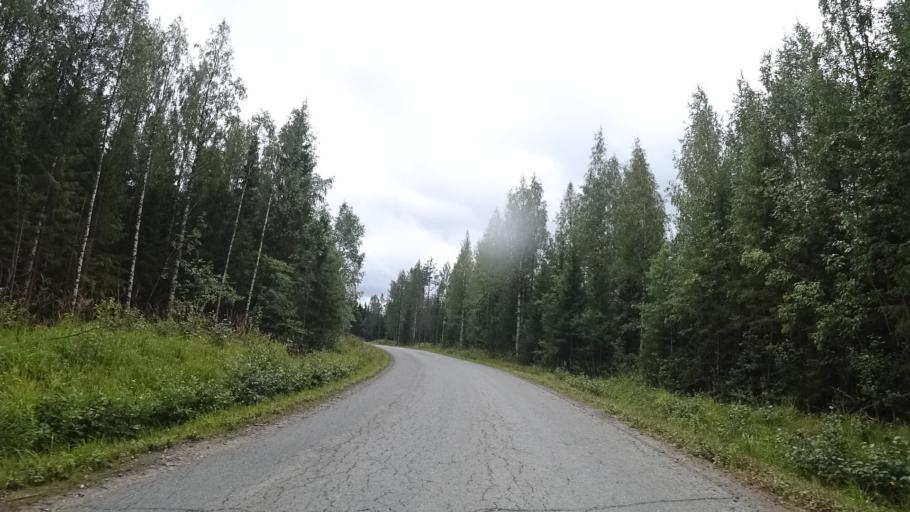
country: FI
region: North Karelia
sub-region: Joensuu
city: Ilomantsi
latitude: 62.9925
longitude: 31.2795
